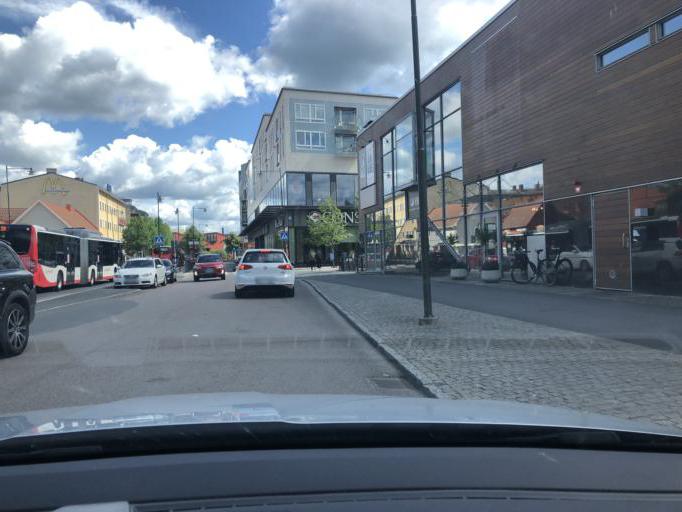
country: SE
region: Joenkoeping
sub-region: Jonkopings Kommun
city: Jonkoping
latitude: 57.7814
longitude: 14.1710
